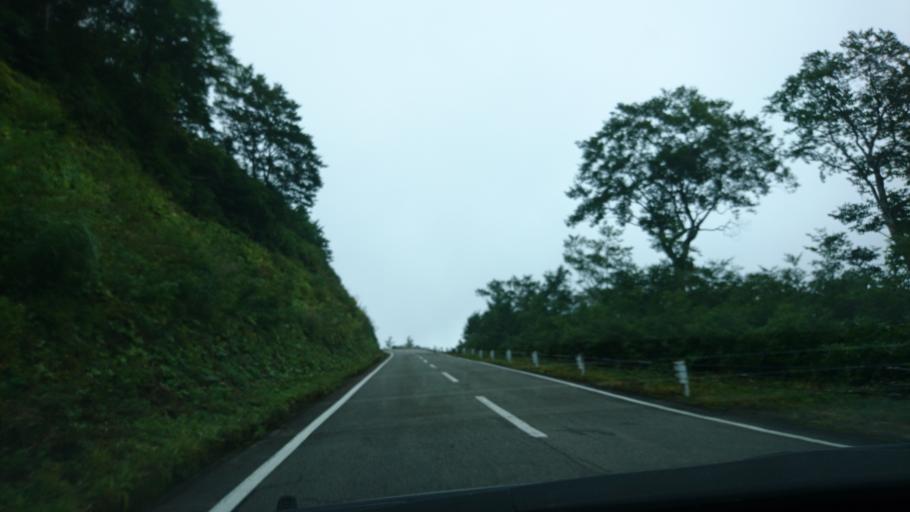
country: JP
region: Akita
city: Yuzawa
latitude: 38.9787
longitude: 140.7556
